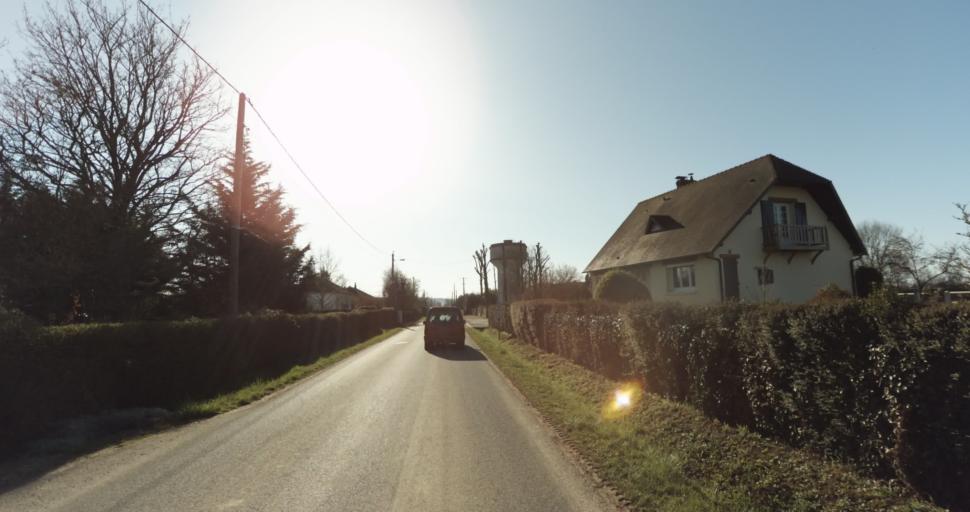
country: FR
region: Lower Normandy
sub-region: Departement du Calvados
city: Saint-Pierre-sur-Dives
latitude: 49.0065
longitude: -0.0125
